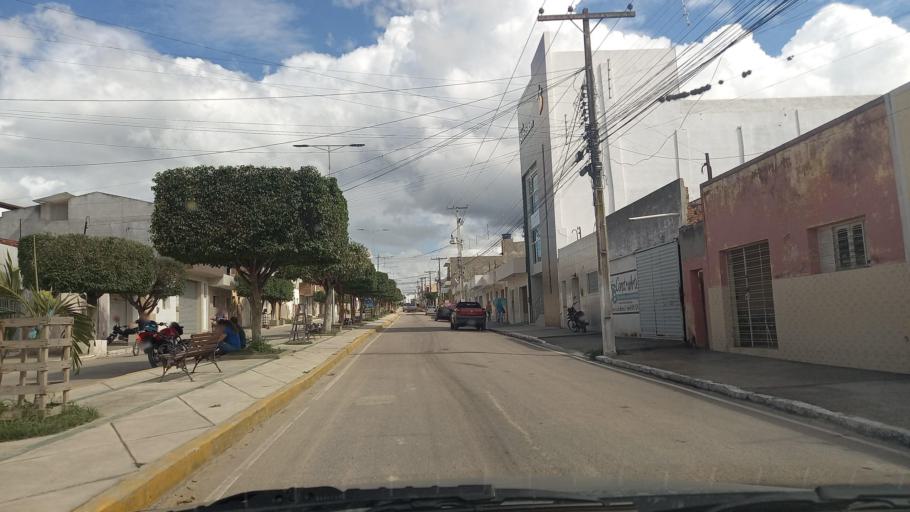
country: BR
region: Pernambuco
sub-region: Cachoeirinha
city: Cachoeirinha
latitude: -8.4893
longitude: -36.2375
